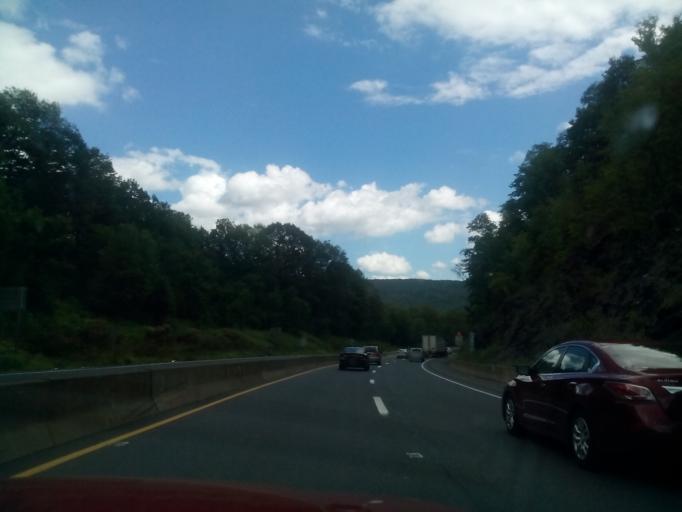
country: US
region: Pennsylvania
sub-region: Monroe County
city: East Stroudsburg
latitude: 40.9977
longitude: -75.1463
